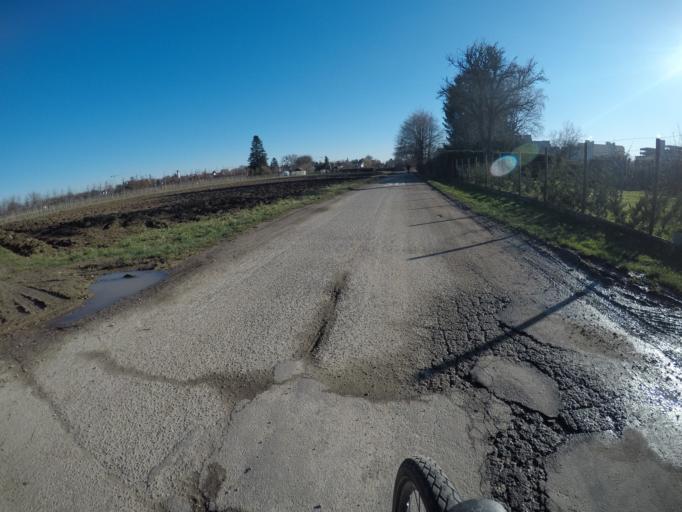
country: DE
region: Baden-Wuerttemberg
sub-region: Regierungsbezirk Stuttgart
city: Leinfelden-Echterdingen
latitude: 48.7358
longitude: 9.1389
